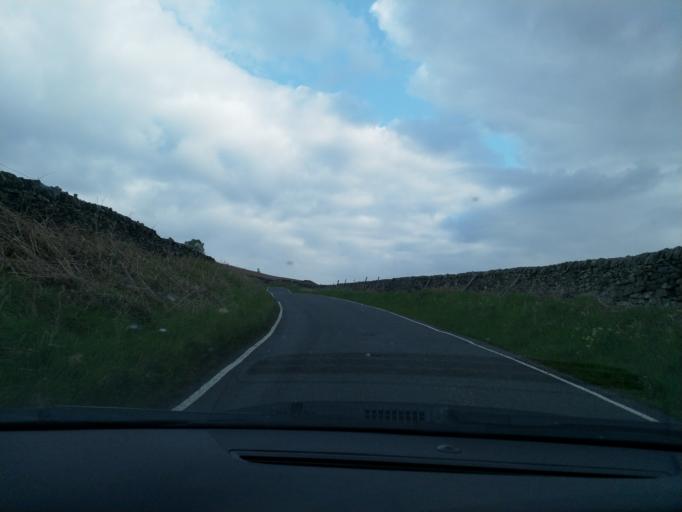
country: GB
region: England
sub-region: Derbyshire
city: Hathersage
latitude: 53.3338
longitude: -1.6302
